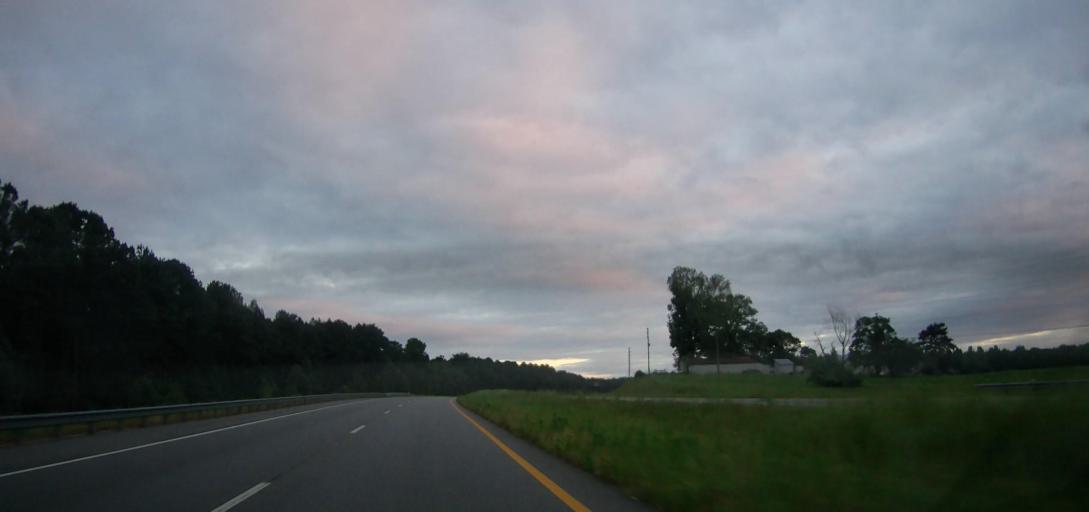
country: US
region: Georgia
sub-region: Jackson County
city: Arcade
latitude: 34.0288
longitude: -83.4958
